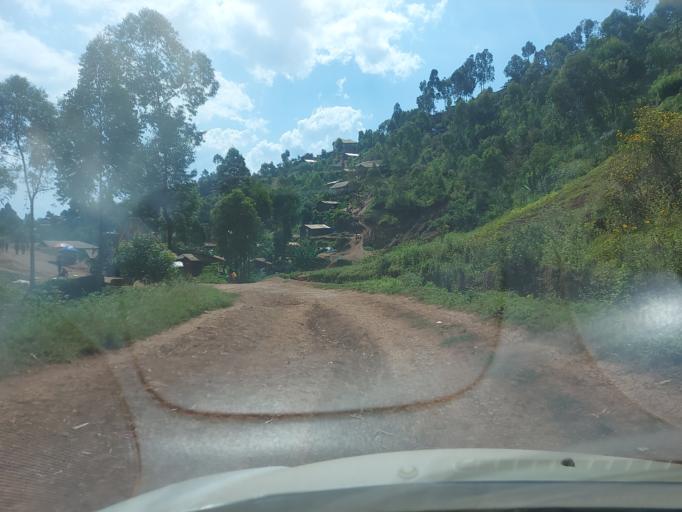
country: CD
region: South Kivu
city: Bukavu
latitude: -2.5132
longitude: 28.8328
